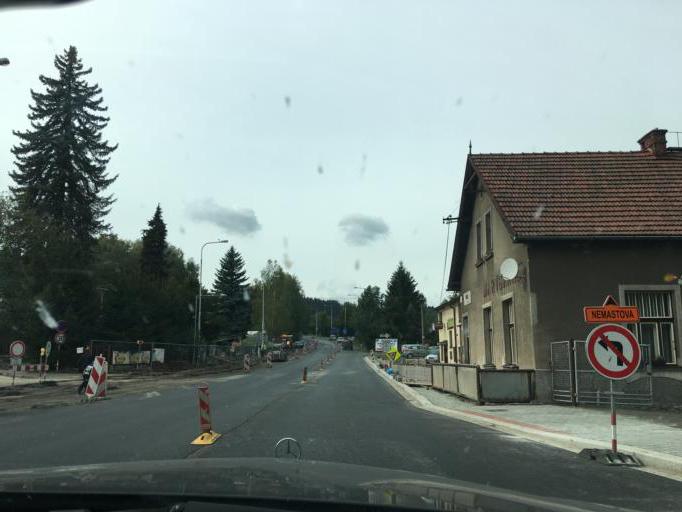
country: CZ
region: Kralovehradecky
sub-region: Okres Nachod
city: Nachod
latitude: 50.4065
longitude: 16.1485
